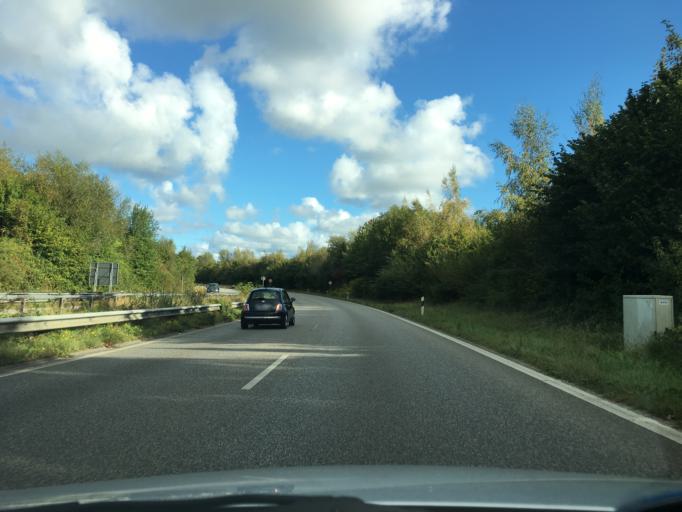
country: DE
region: Schleswig-Holstein
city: Klausdorf
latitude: 54.3319
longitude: 10.2036
